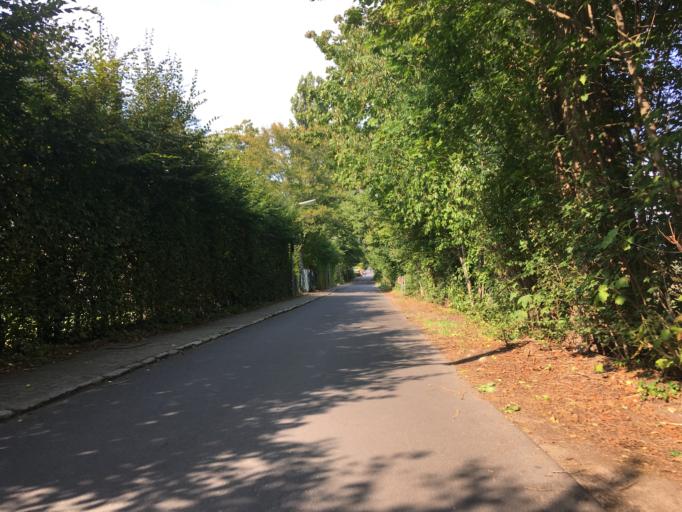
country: DE
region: Berlin
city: Lubars
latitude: 52.6182
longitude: 13.3393
